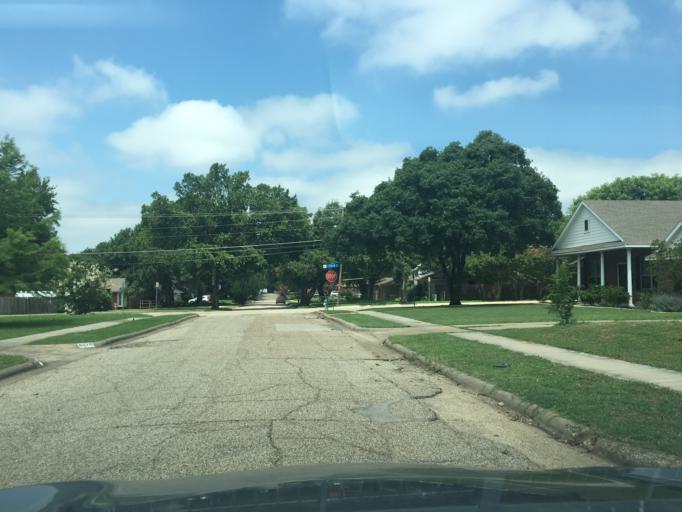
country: US
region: Texas
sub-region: Dallas County
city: Richardson
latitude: 32.9453
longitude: -96.7434
